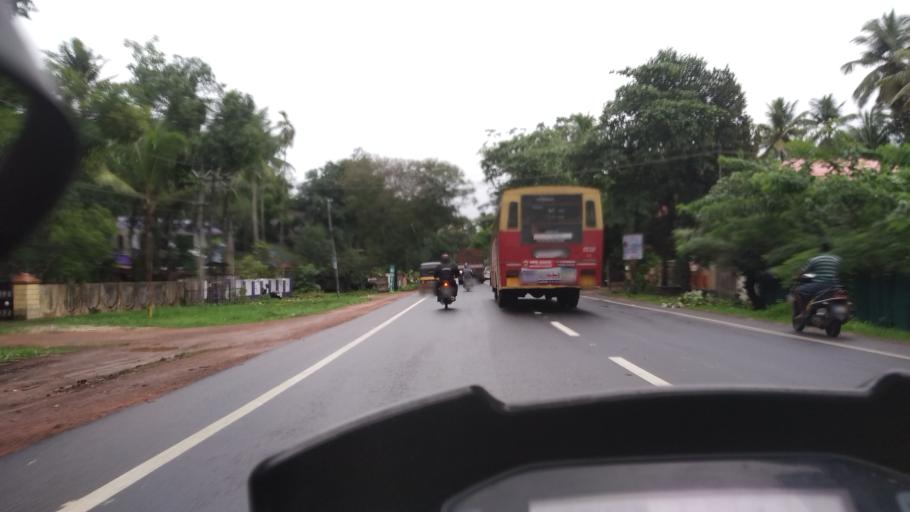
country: IN
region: Kerala
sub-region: Alappuzha
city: Mavelikara
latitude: 9.2905
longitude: 76.4364
